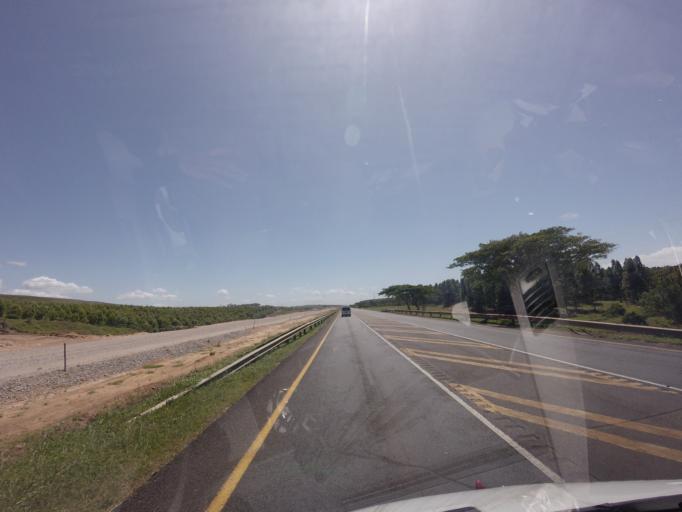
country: ZA
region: KwaZulu-Natal
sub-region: uThungulu District Municipality
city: eSikhawini
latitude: -28.9149
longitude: 31.8088
